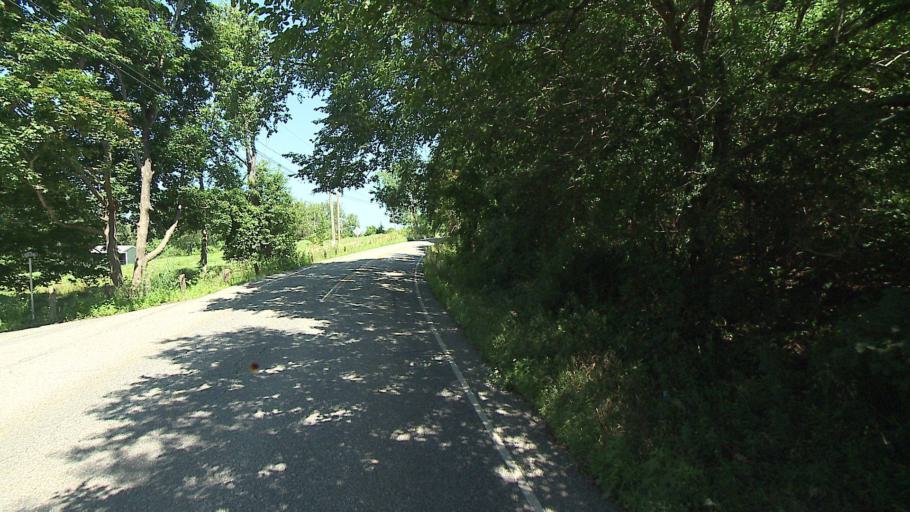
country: US
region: New York
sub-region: Dutchess County
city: Pine Plains
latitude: 41.9067
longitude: -73.4924
